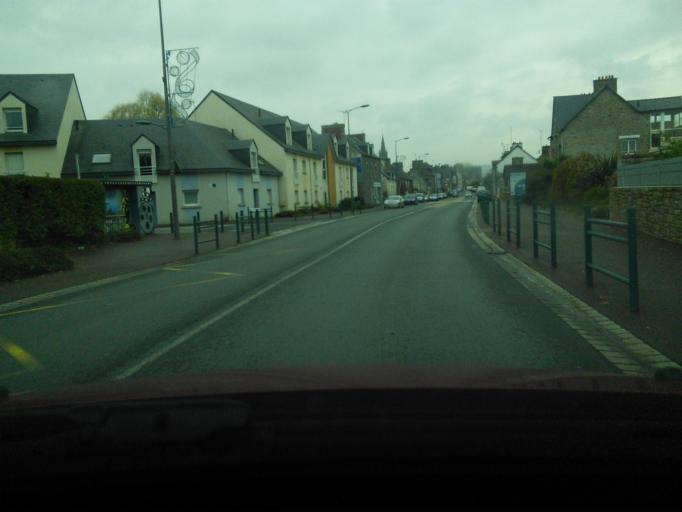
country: FR
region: Brittany
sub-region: Departement des Cotes-d'Armor
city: Yffiniac
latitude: 48.4853
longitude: -2.6725
